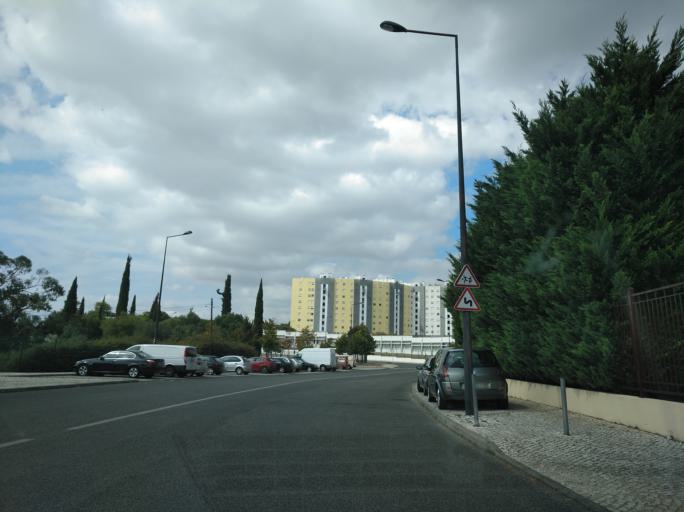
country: PT
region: Lisbon
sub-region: Lisbon
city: Lisbon
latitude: 38.7428
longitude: -9.1201
